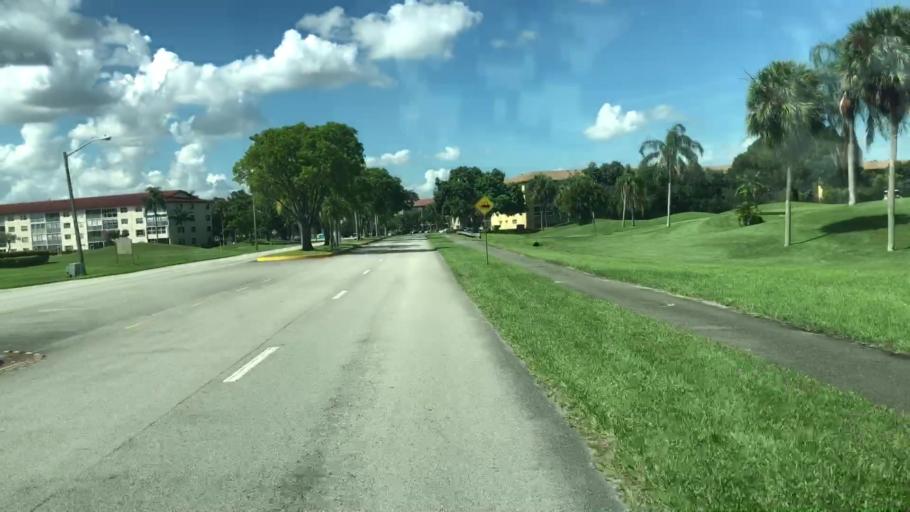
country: US
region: Florida
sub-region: Broward County
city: Sunshine Ranches
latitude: 26.0031
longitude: -80.3209
